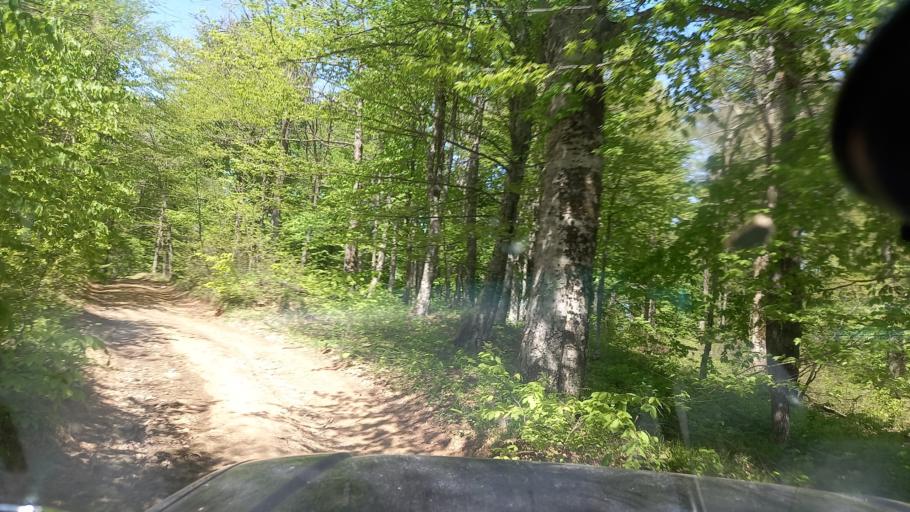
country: RU
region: Krasnodarskiy
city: Shepsi
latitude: 44.2471
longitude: 39.2985
